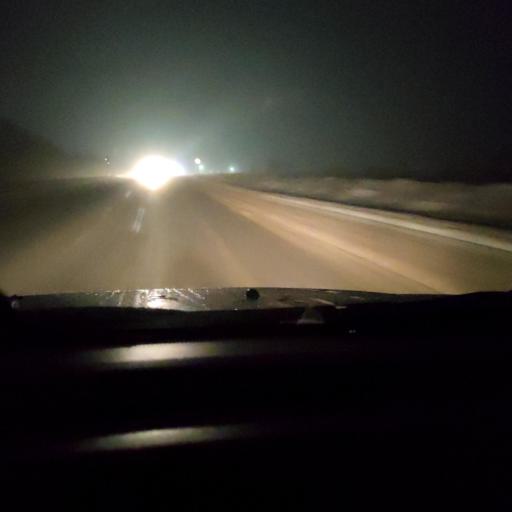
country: RU
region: Samara
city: Dubovyy Umet
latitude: 53.0057
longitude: 50.2469
